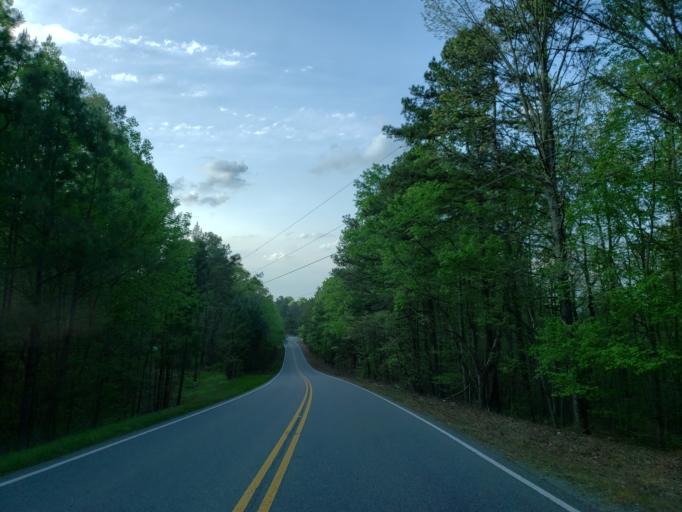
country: US
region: Georgia
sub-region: Cherokee County
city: Ball Ground
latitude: 34.2729
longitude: -84.3715
